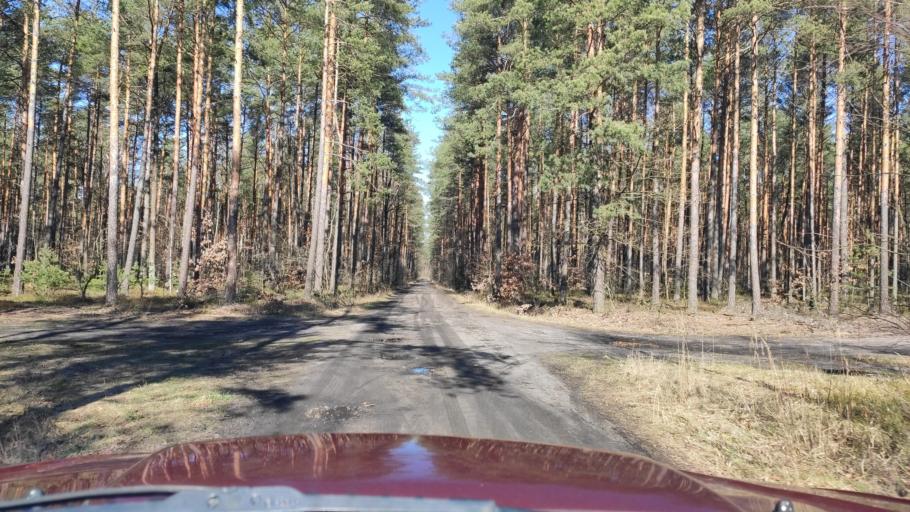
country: PL
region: Masovian Voivodeship
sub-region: Powiat kozienicki
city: Garbatka-Letnisko
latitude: 51.4306
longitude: 21.5482
